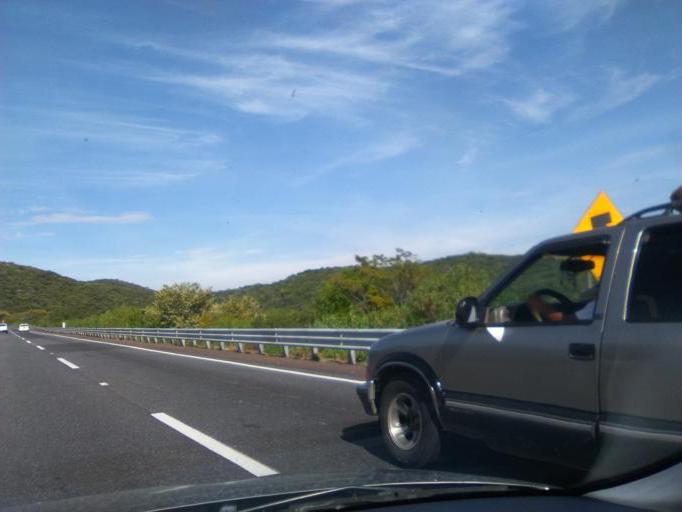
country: MX
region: Guerrero
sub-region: Huitzuco de los Figueroa
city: Ciudad de Huitzuco
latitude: 18.2632
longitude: -99.2086
